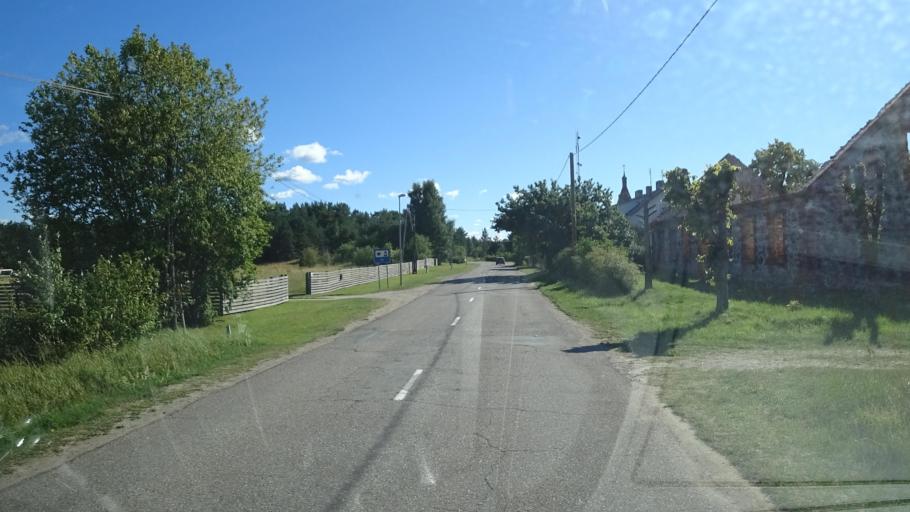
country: LV
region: Rojas
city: Roja
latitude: 57.7495
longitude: 22.5939
